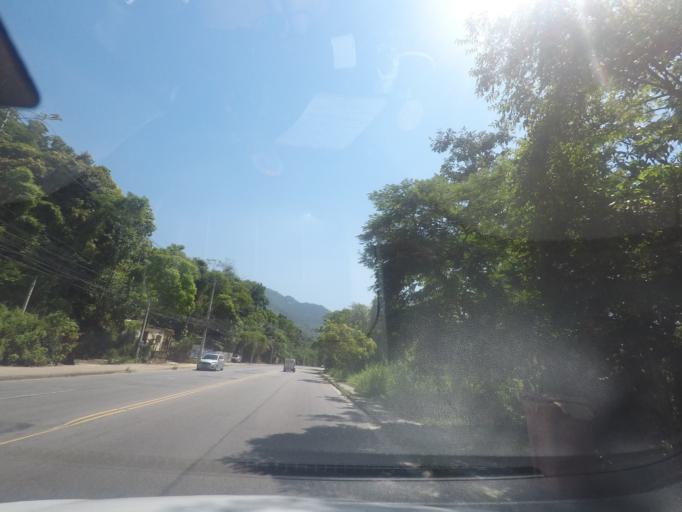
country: BR
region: Rio de Janeiro
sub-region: Nilopolis
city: Nilopolis
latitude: -22.9859
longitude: -43.4750
